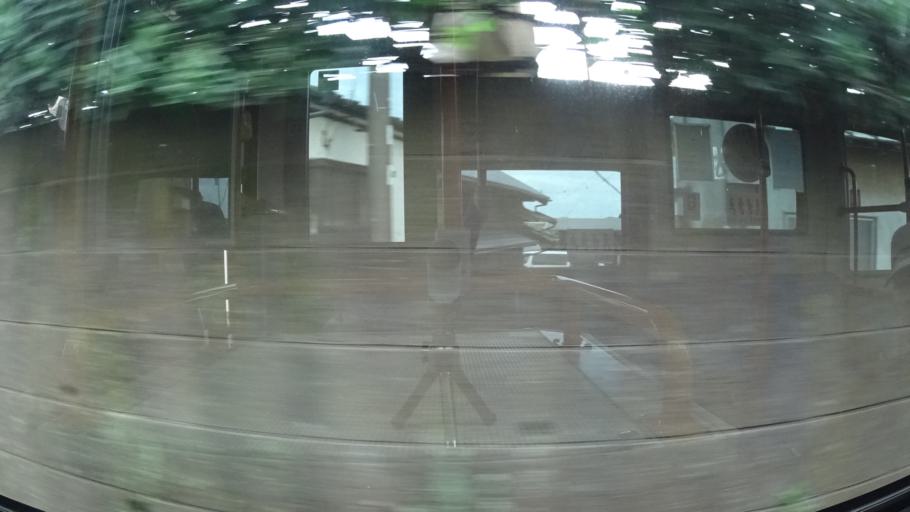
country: JP
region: Kanagawa
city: Miura
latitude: 35.1444
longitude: 139.6537
